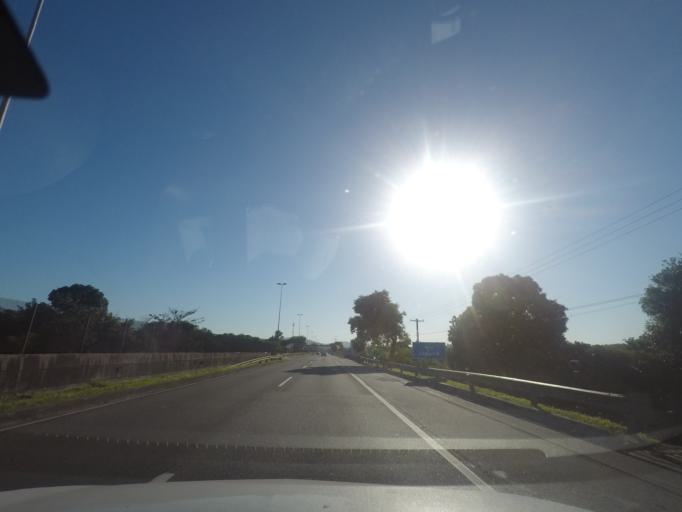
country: BR
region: Rio de Janeiro
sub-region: Petropolis
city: Petropolis
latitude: -22.6468
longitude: -43.2142
